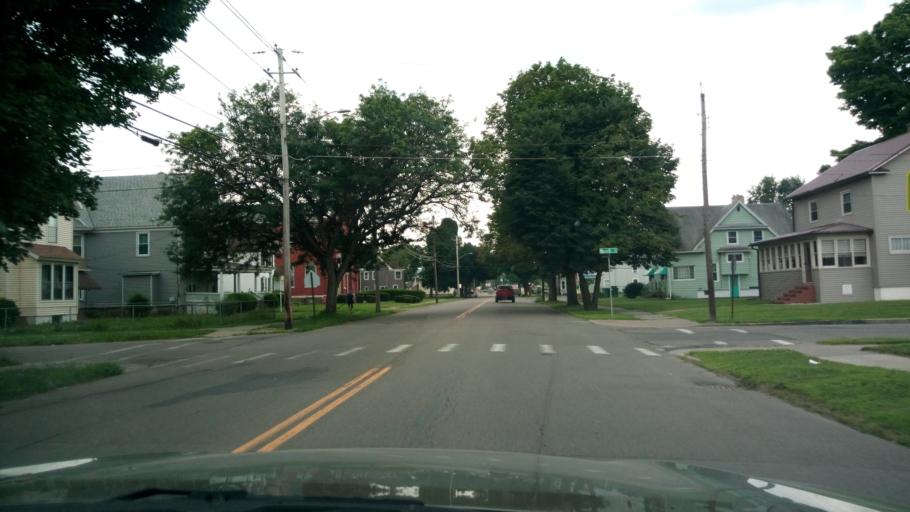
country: US
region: New York
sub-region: Chemung County
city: Elmira
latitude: 42.1044
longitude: -76.8049
